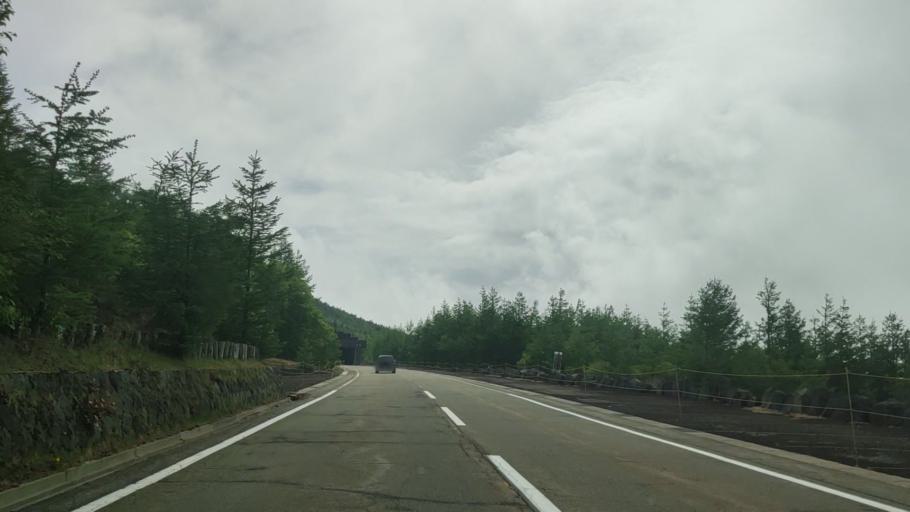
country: JP
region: Yamanashi
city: Fujikawaguchiko
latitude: 35.3904
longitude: 138.7130
